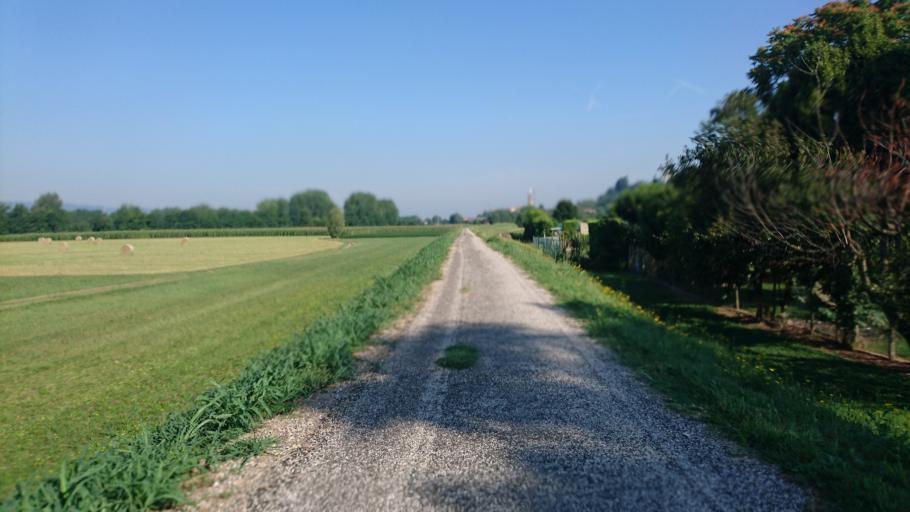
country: IT
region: Veneto
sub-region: Provincia di Padova
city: Cervarese Santa Croce
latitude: 45.4351
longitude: 11.6836
